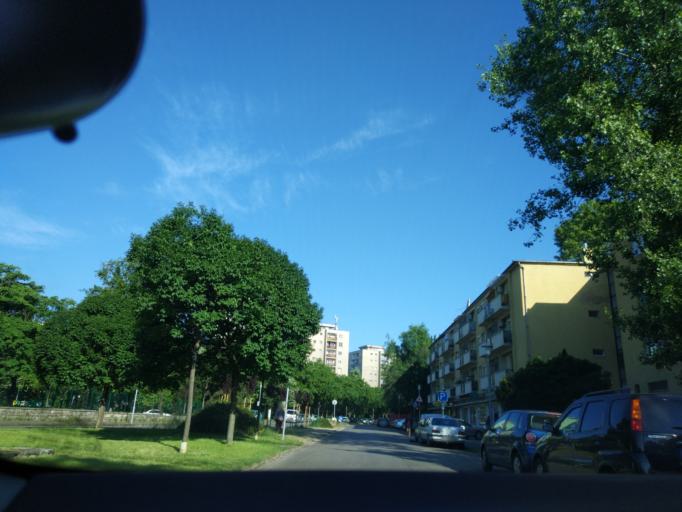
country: HU
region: Budapest
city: Budapest XX. keruelet
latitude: 47.4656
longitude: 19.1146
